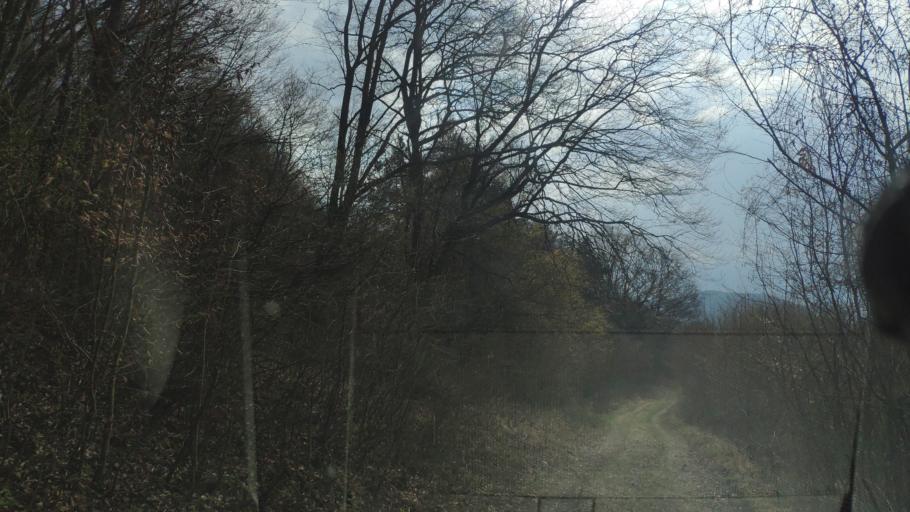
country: SK
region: Kosicky
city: Roznava
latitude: 48.6239
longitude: 20.3890
